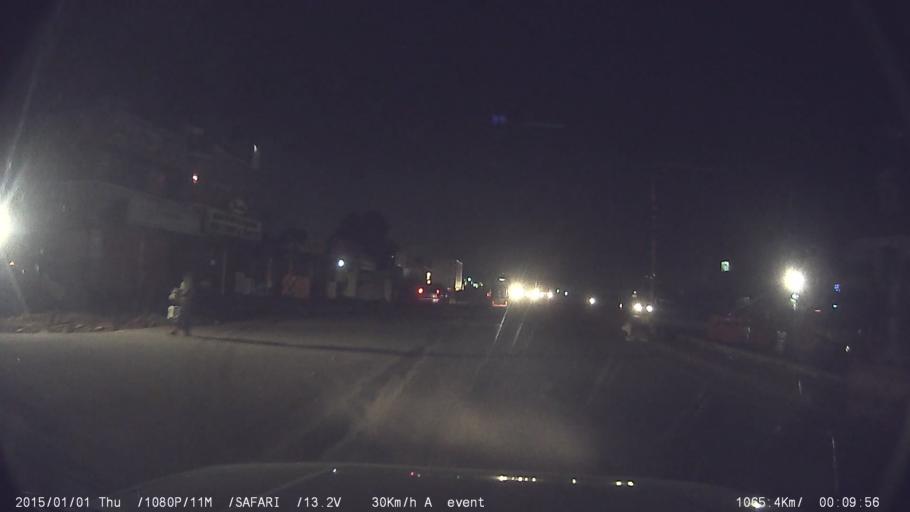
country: IN
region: Tamil Nadu
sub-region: Thiruvallur
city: Porur
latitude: 13.0612
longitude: 80.1641
